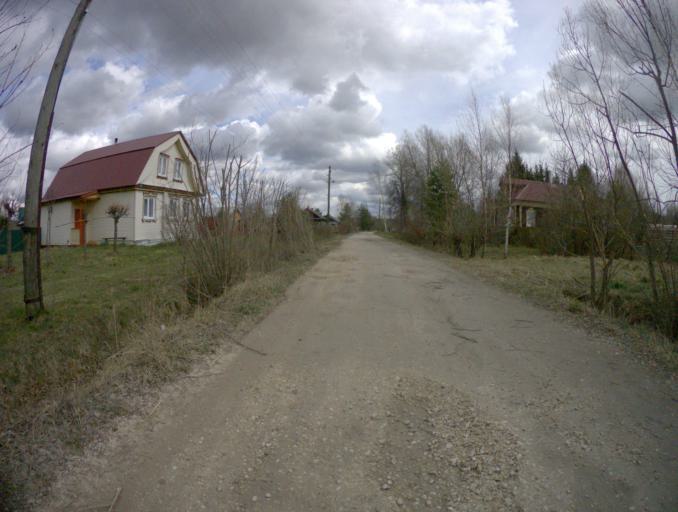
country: RU
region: Vladimir
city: Sudogda
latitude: 56.0757
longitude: 40.7596
